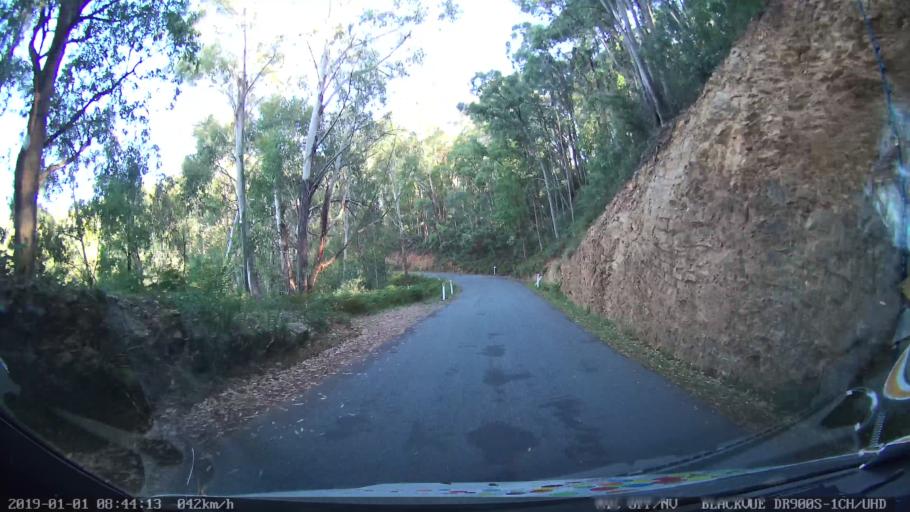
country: AU
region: New South Wales
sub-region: Snowy River
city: Jindabyne
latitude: -36.3121
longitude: 148.1900
